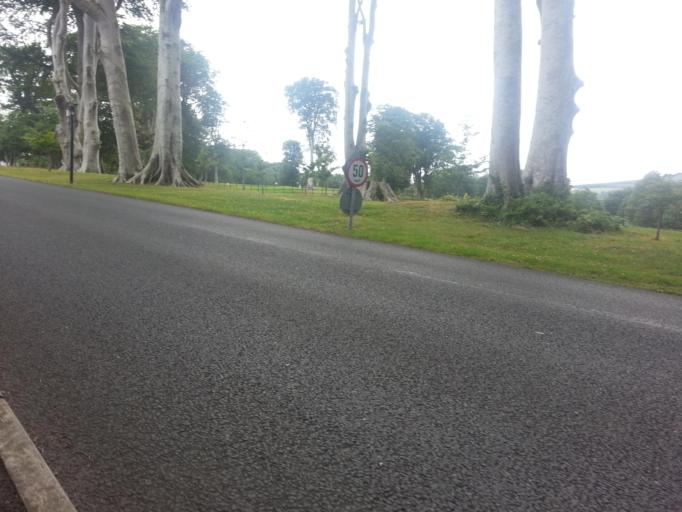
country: IE
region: Leinster
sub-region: Wicklow
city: Enniskerry
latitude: 53.1872
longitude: -6.1719
